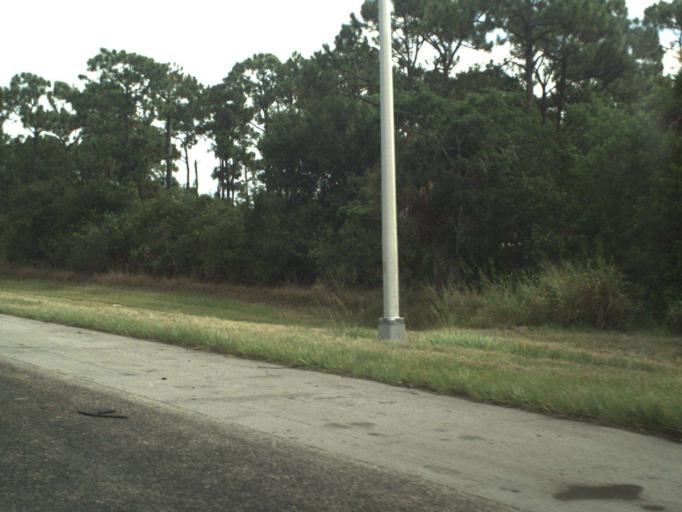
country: US
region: Florida
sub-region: Saint Lucie County
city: Fort Pierce South
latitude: 27.4294
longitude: -80.3882
